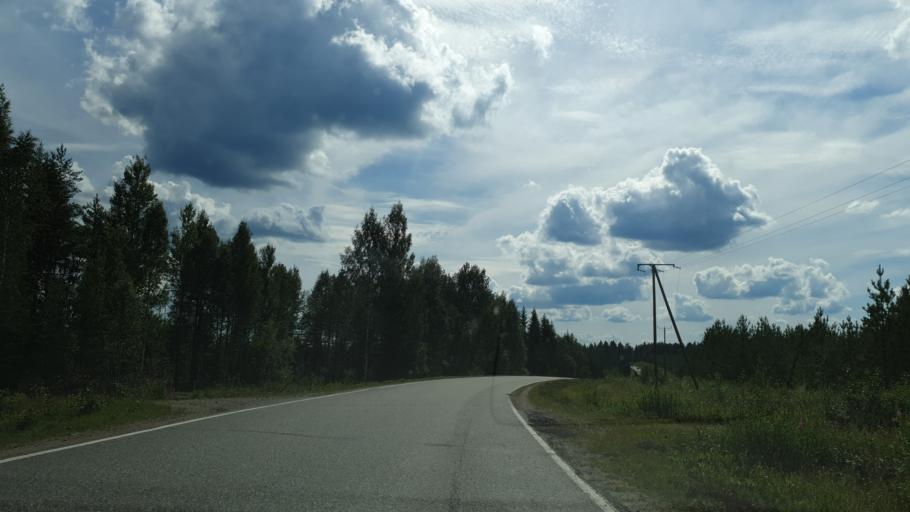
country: FI
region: Kainuu
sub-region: Kajaani
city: Sotkamo
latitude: 64.1828
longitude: 28.4624
